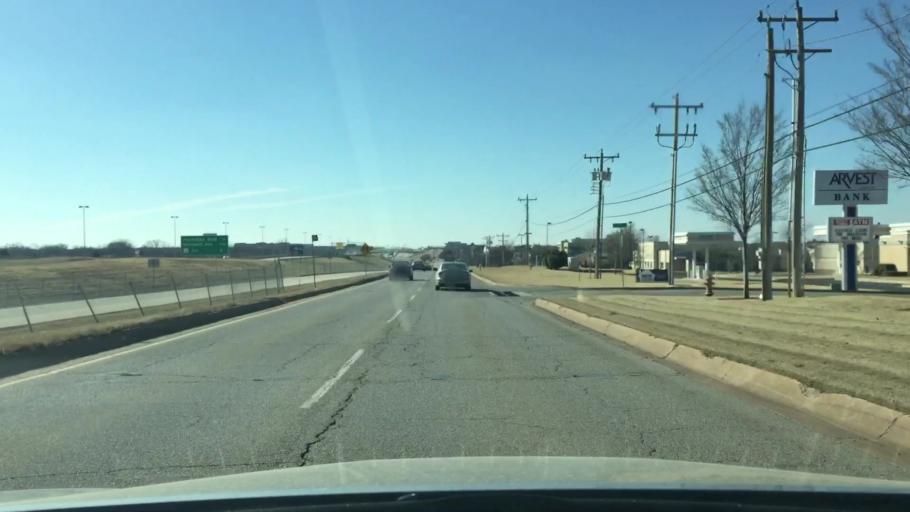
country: US
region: Oklahoma
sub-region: Oklahoma County
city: The Village
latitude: 35.6103
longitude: -97.5977
